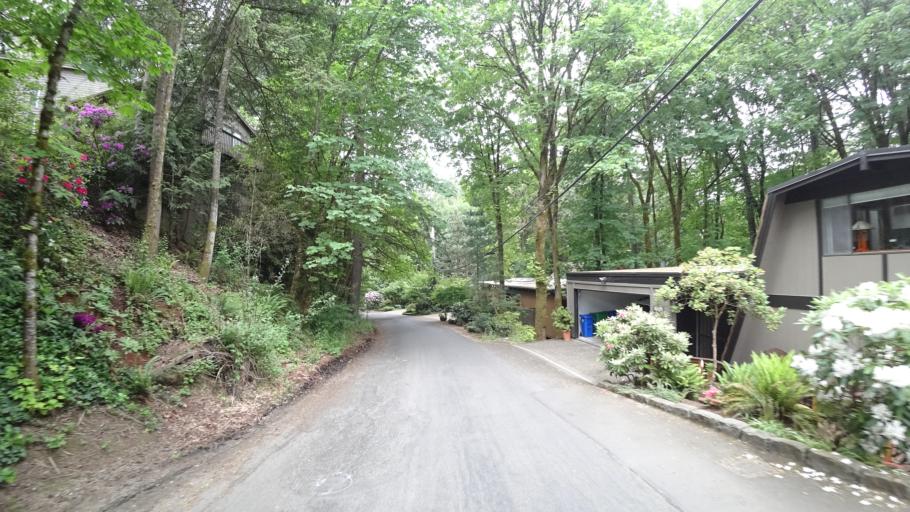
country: US
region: Oregon
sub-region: Multnomah County
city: Portland
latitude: 45.5018
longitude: -122.7000
